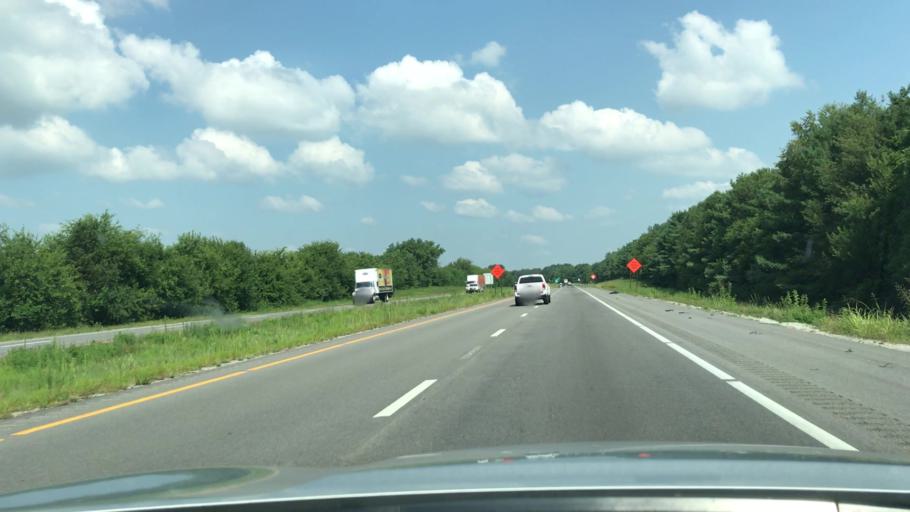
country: US
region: Kentucky
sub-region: Warren County
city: Plano
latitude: 36.9279
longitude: -86.4549
